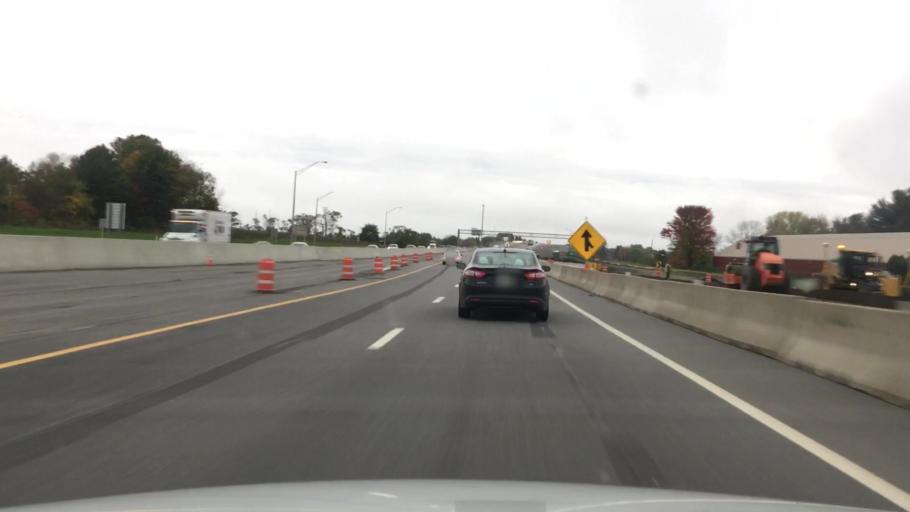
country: US
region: Maine
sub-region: York County
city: South Eliot
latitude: 43.1132
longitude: -70.8195
